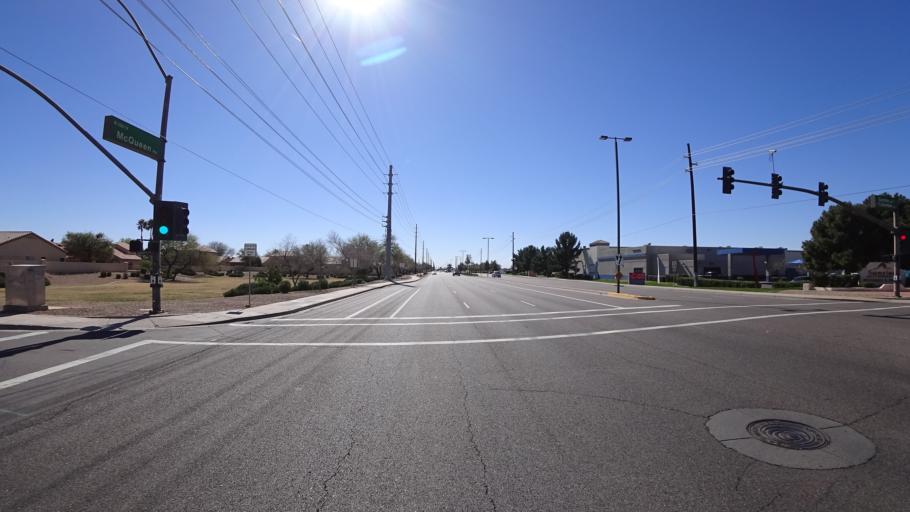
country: US
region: Arizona
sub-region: Maricopa County
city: San Carlos
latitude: 33.3550
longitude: -111.8243
